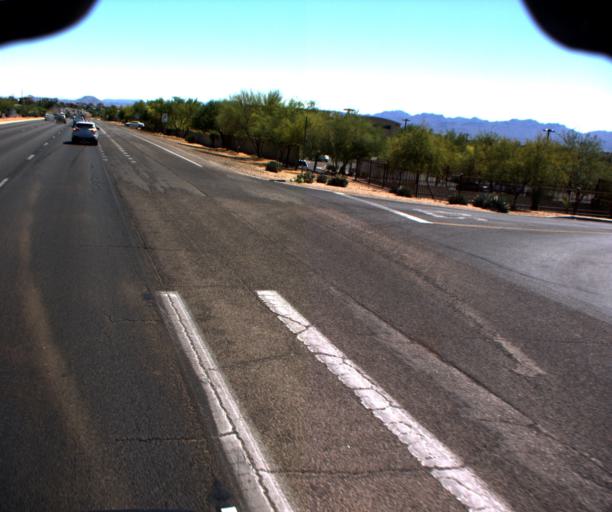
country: US
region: Arizona
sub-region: Pima County
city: Casas Adobes
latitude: 32.3491
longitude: -110.9756
